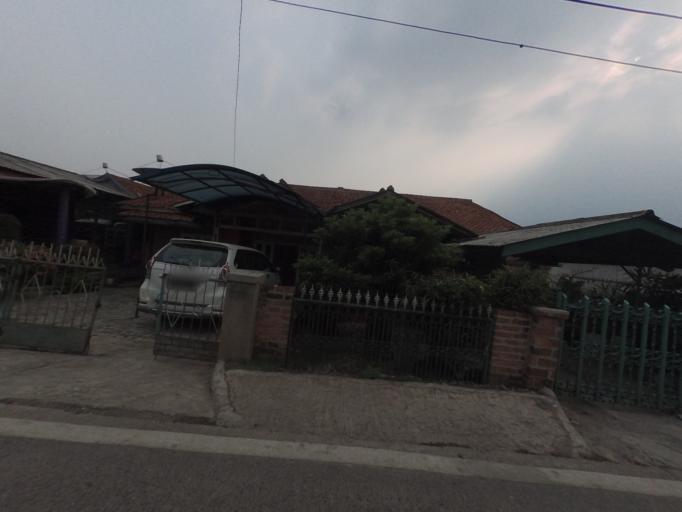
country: ID
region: West Java
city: Sidoger Lebak
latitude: -6.5656
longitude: 106.5928
